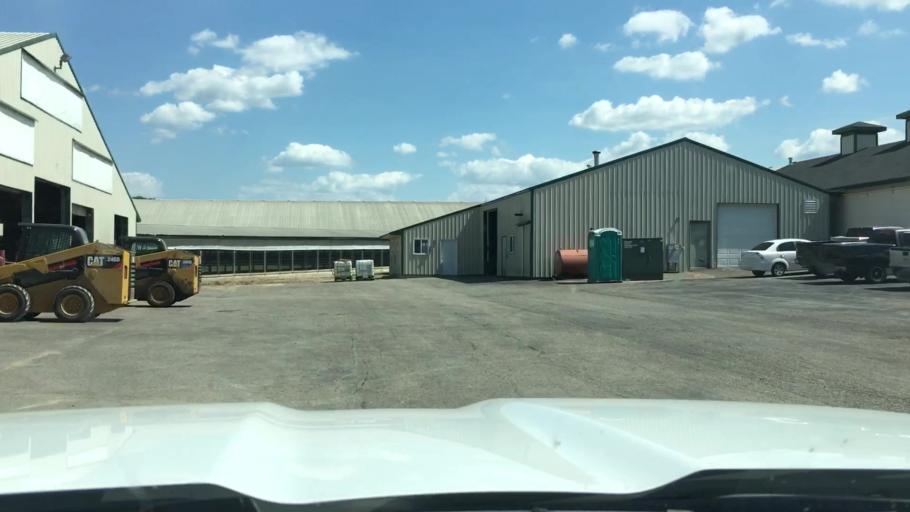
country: US
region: Michigan
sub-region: Muskegon County
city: Ravenna
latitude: 43.2956
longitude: -85.9050
